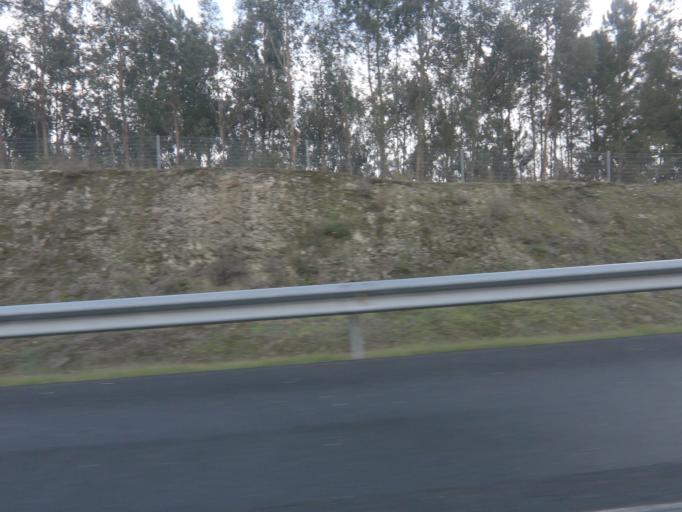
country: ES
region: Galicia
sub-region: Provincia da Coruna
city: Ribeira
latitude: 42.7365
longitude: -8.3672
